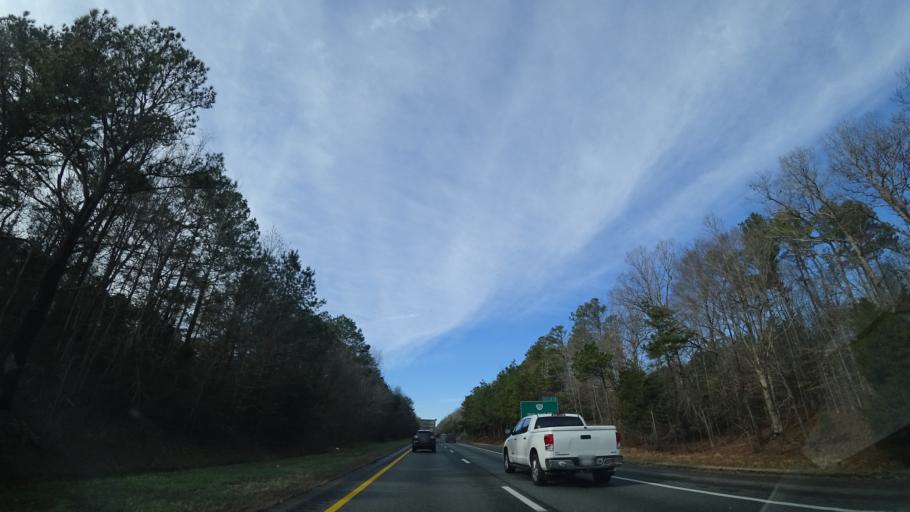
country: US
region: Virginia
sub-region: New Kent County
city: New Kent
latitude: 37.4906
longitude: -76.9977
